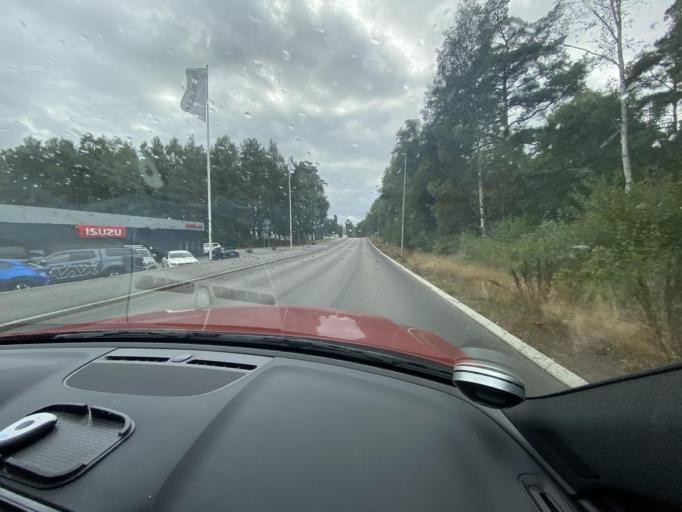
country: SE
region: Kronoberg
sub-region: Markaryds Kommun
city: Markaryd
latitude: 56.4517
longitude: 13.6084
